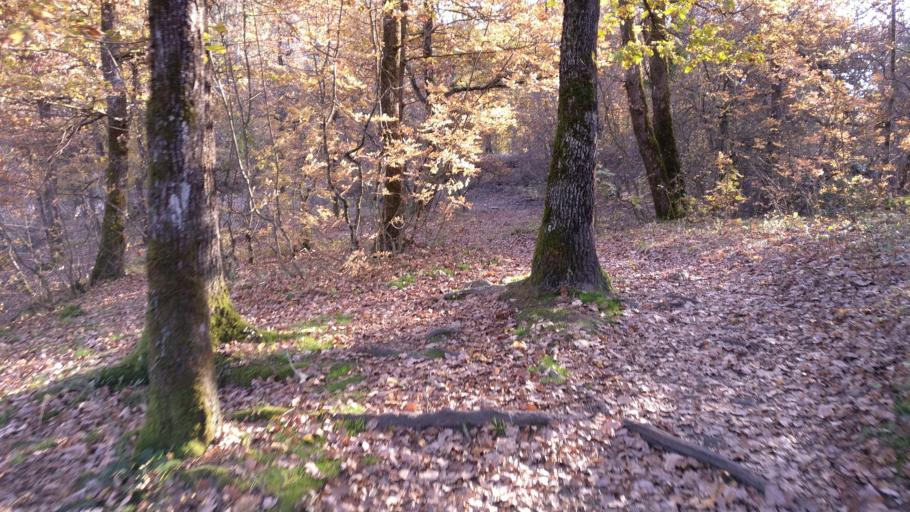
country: IT
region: Trentino-Alto Adige
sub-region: Bolzano
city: Vadena
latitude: 46.4287
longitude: 11.2954
